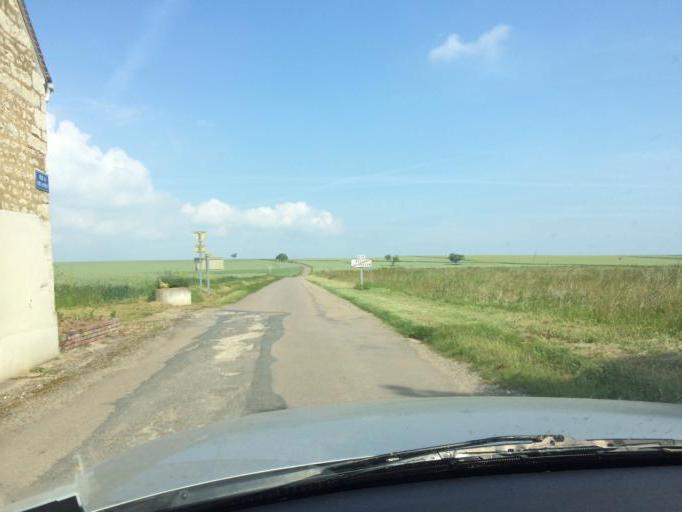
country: FR
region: Bourgogne
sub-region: Departement de l'Yonne
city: Aillant-sur-Tholon
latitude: 47.8663
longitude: 3.3933
